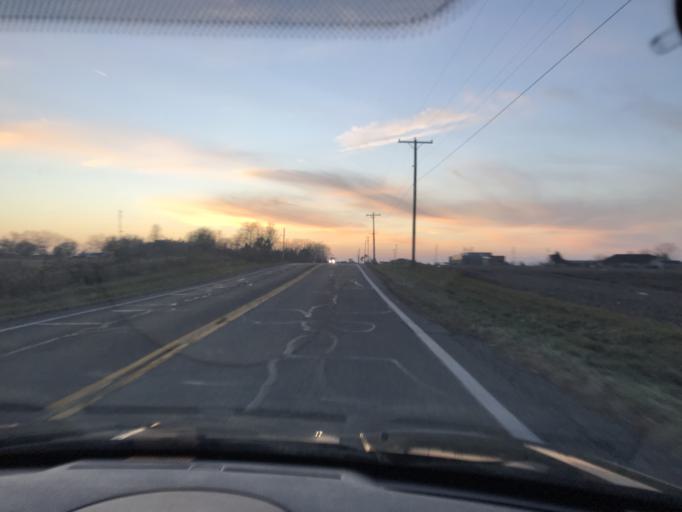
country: US
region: Ohio
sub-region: Champaign County
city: Urbana
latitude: 40.1074
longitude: -83.7087
